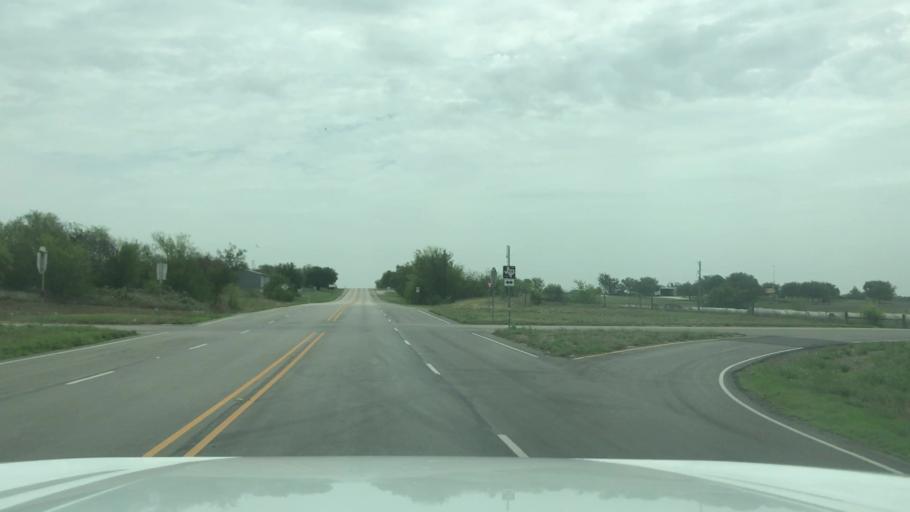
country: US
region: Texas
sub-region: Erath County
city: Dublin
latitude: 32.0590
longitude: -98.2069
